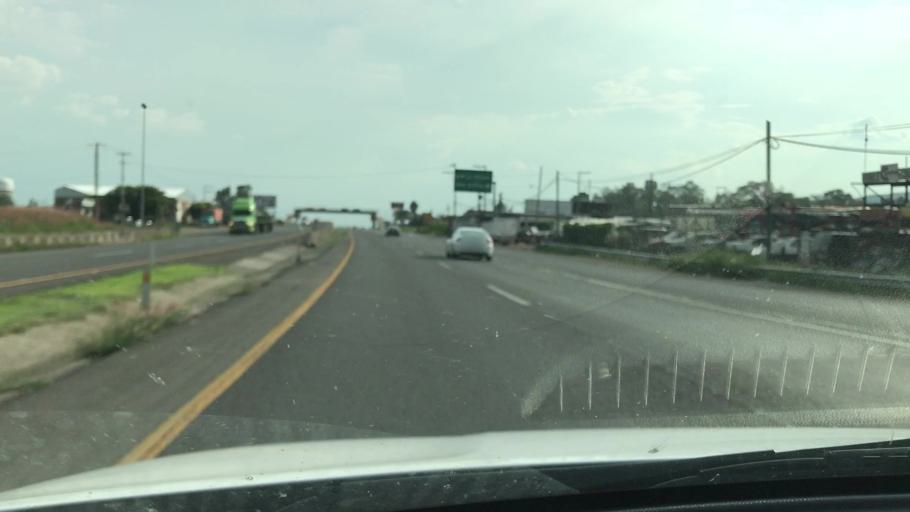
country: MX
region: Guanajuato
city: Penjamo
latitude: 20.4184
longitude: -101.7257
